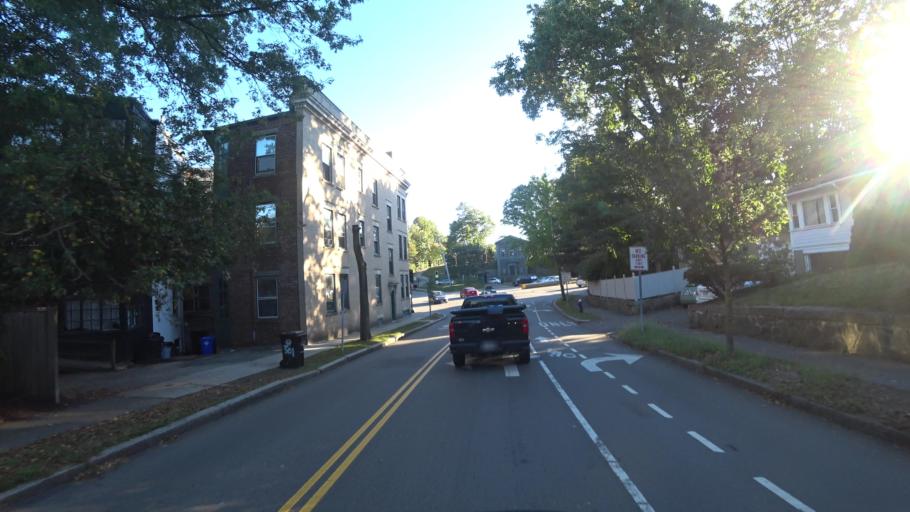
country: US
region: Massachusetts
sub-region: Norfolk County
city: Brookline
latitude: 42.3294
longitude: -71.1328
